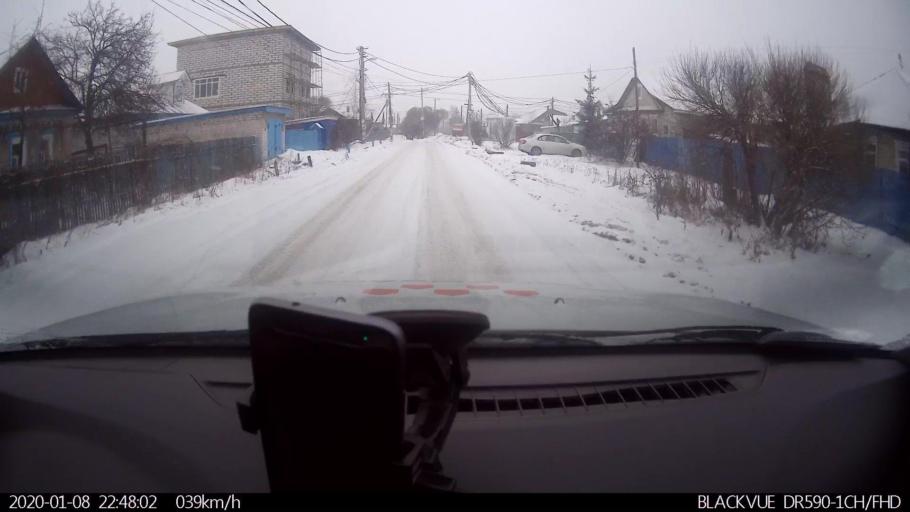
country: RU
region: Nizjnij Novgorod
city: Nizhniy Novgorod
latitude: 56.2896
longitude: 43.8945
